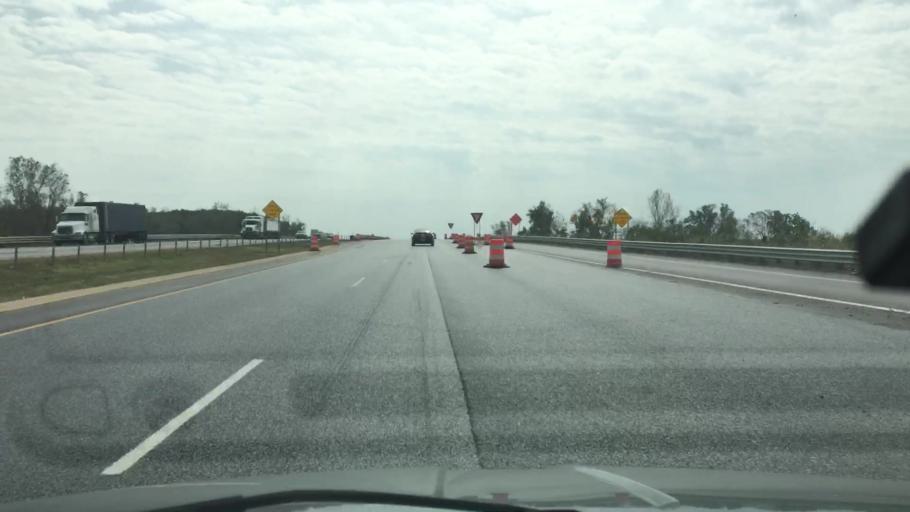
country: US
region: Michigan
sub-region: Berrien County
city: Shorewood-Tower Hills-Harbert
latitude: 41.8824
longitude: -86.6016
